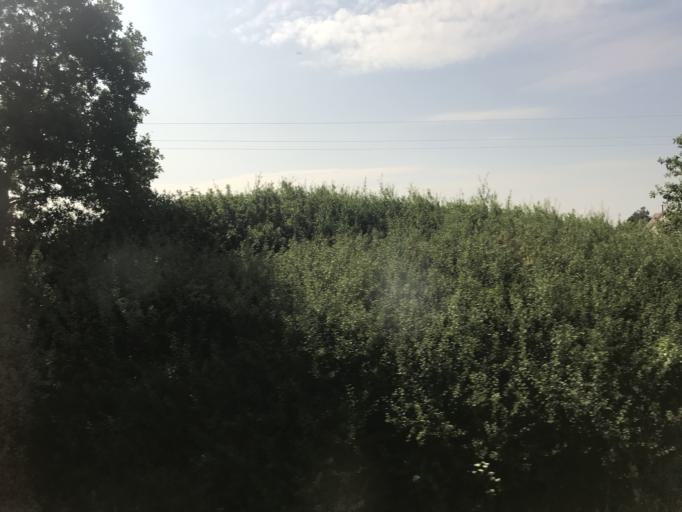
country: PL
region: Kujawsko-Pomorskie
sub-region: Powiat swiecki
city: Bukowiec
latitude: 53.3751
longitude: 18.2829
